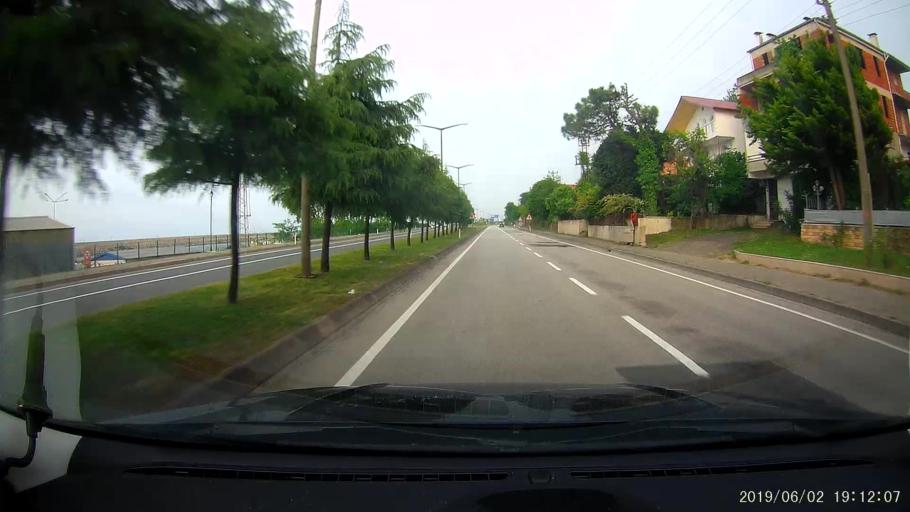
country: TR
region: Ordu
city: Gulyali
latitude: 40.9662
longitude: 38.0635
